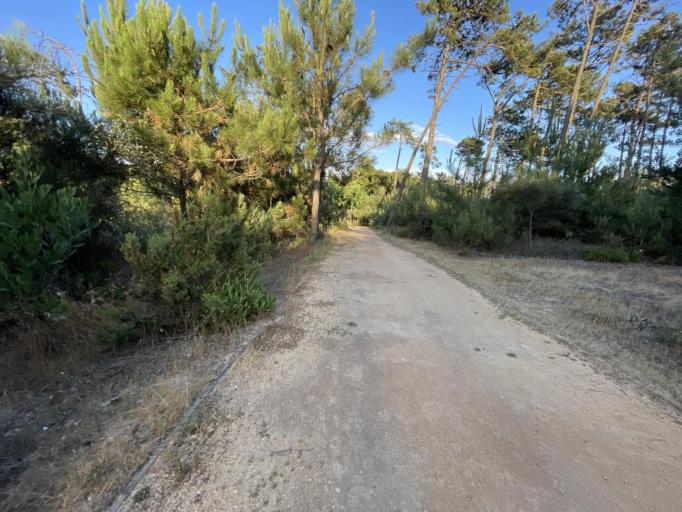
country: PT
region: Aveiro
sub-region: Ovar
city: Esmoriz
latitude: 40.9479
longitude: -8.6401
